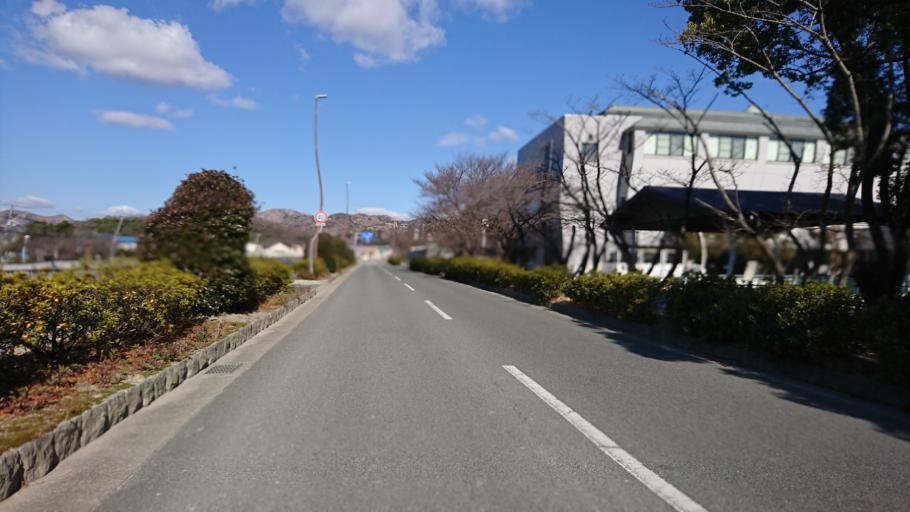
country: JP
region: Hyogo
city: Kakogawacho-honmachi
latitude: 34.7814
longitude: 134.7978
